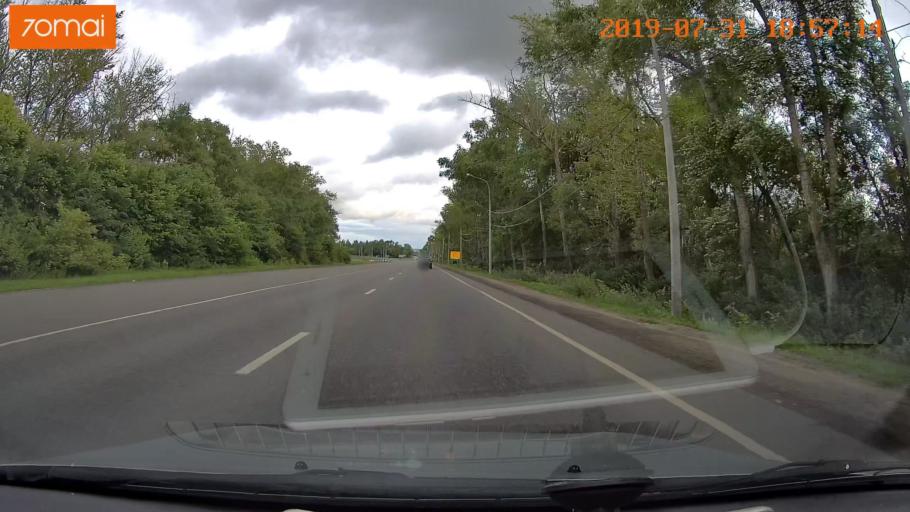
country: RU
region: Moskovskaya
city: Raduzhnyy
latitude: 55.1557
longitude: 38.6895
